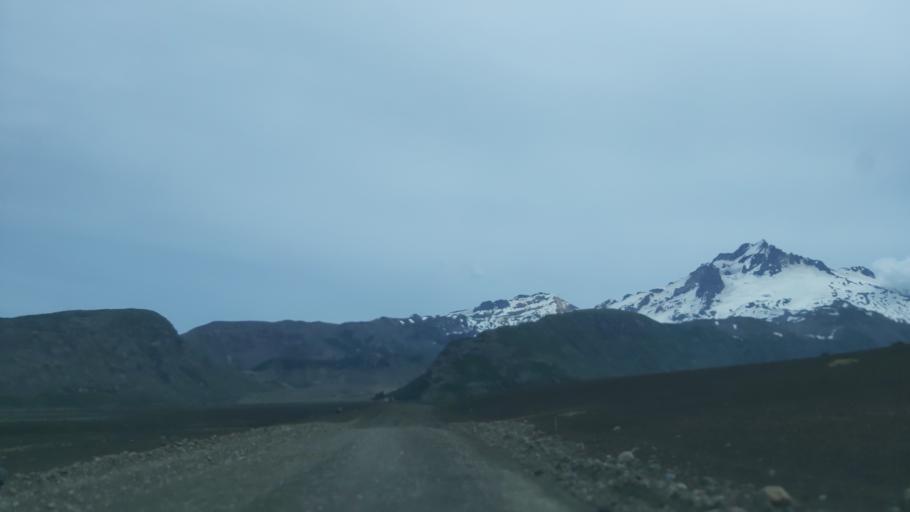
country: AR
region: Neuquen
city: Andacollo
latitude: -37.4578
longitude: -71.2995
